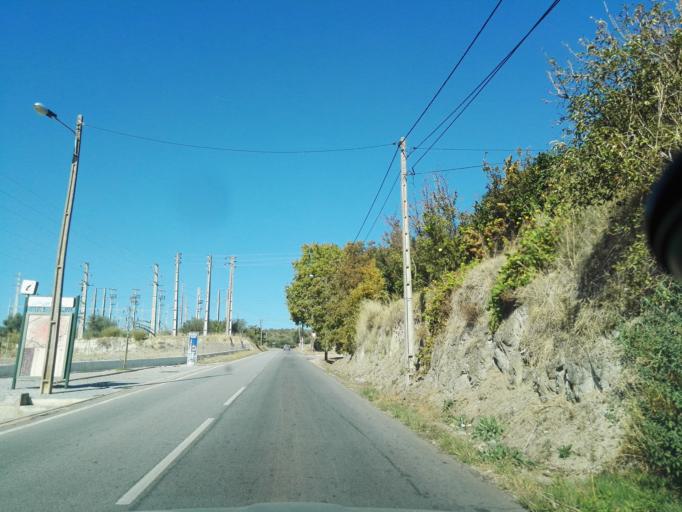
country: PT
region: Portalegre
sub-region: Elvas
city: Elvas
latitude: 38.8864
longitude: -7.1675
